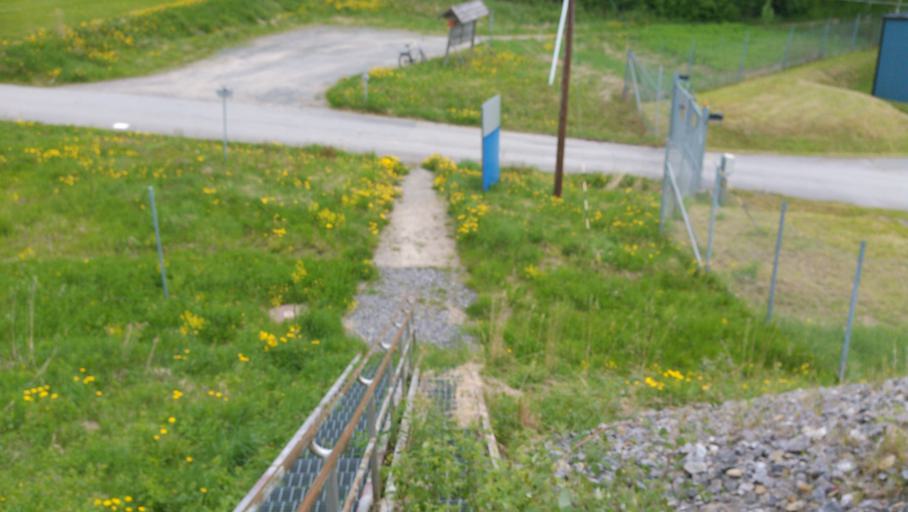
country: SE
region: Vaesterbotten
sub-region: Umea Kommun
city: Roback
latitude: 63.8816
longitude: 20.0210
